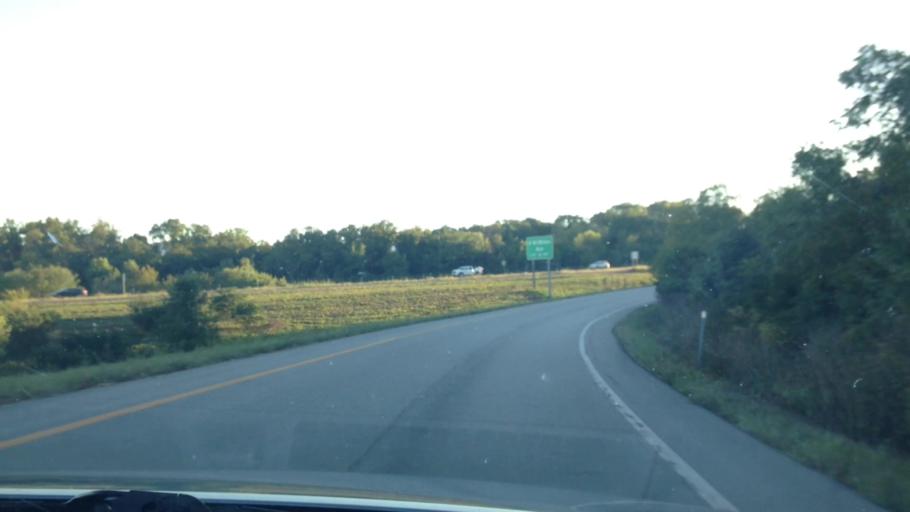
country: US
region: Missouri
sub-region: Clay County
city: Pleasant Valley
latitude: 39.2442
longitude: -94.5110
